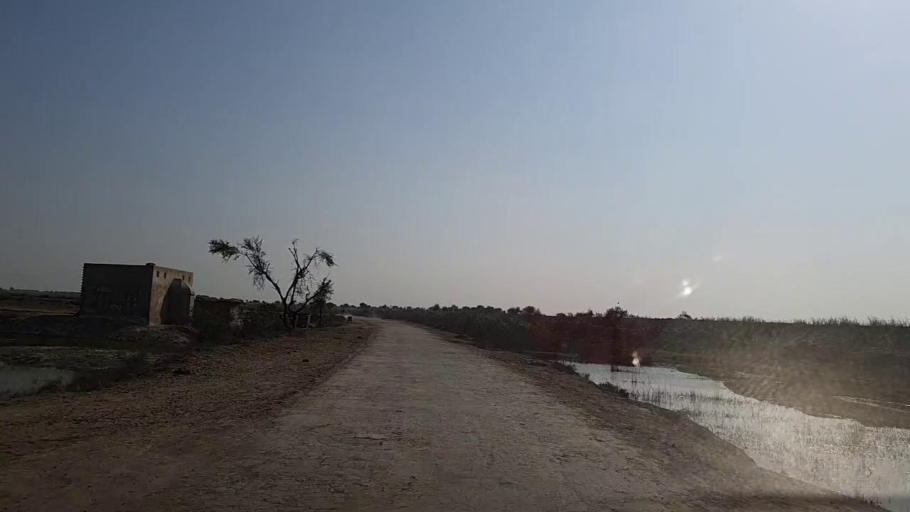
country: PK
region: Sindh
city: Sanghar
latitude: 25.9857
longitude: 69.0226
